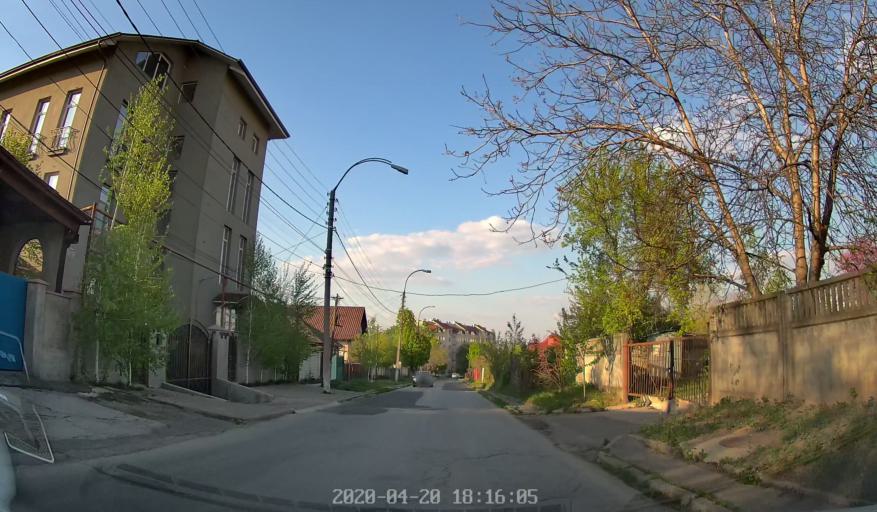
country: MD
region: Chisinau
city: Chisinau
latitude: 46.9995
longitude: 28.8329
